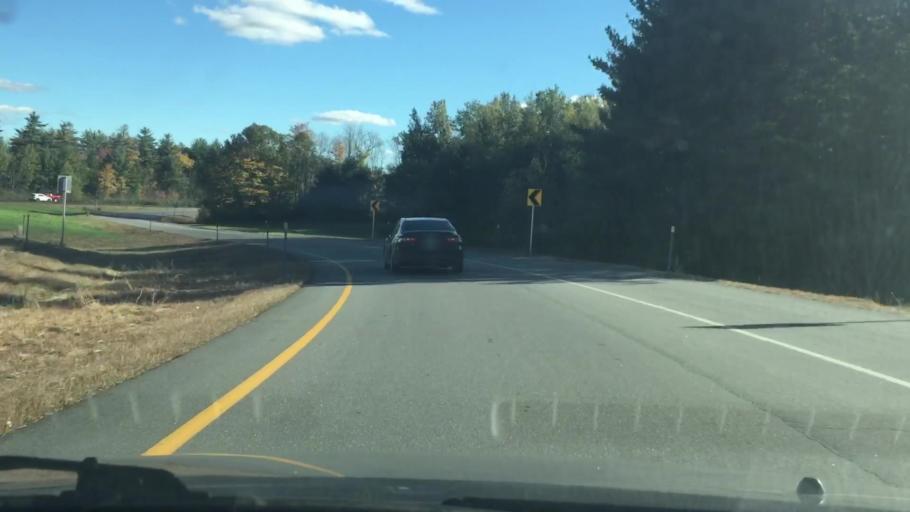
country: US
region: New Hampshire
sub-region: Cheshire County
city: Keene
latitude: 42.9424
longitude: -72.2975
